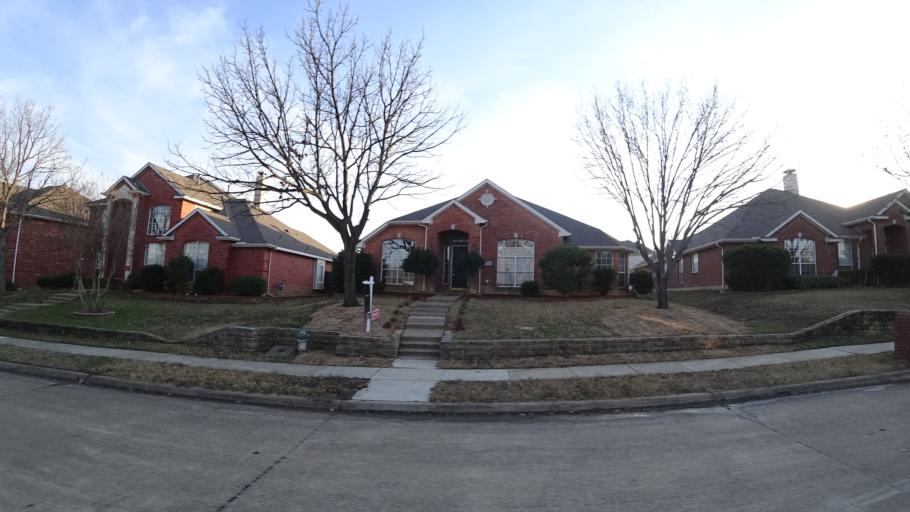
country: US
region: Texas
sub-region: Dallas County
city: Coppell
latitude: 32.9939
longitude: -96.9847
